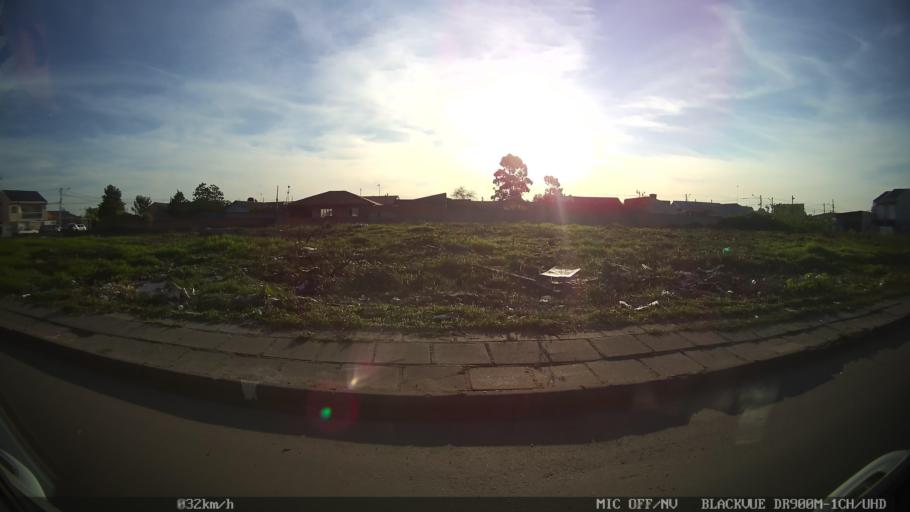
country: BR
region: Parana
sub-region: Pinhais
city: Pinhais
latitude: -25.4519
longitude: -49.1446
